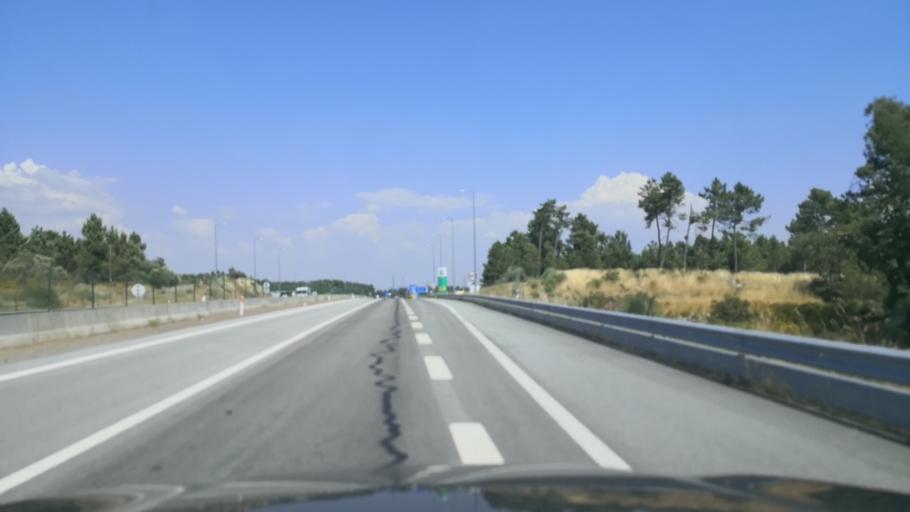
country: PT
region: Vila Real
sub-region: Sabrosa
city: Sabrosa
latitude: 41.3234
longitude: -7.6431
